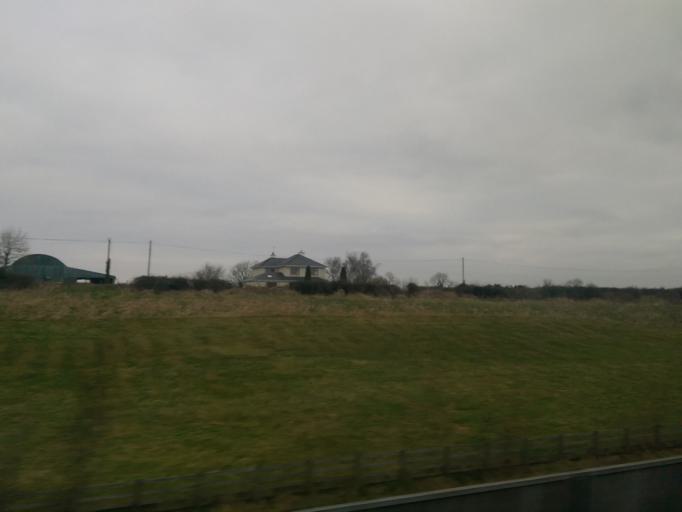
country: IE
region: Connaught
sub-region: County Galway
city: Ballinasloe
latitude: 53.3132
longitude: -8.1972
